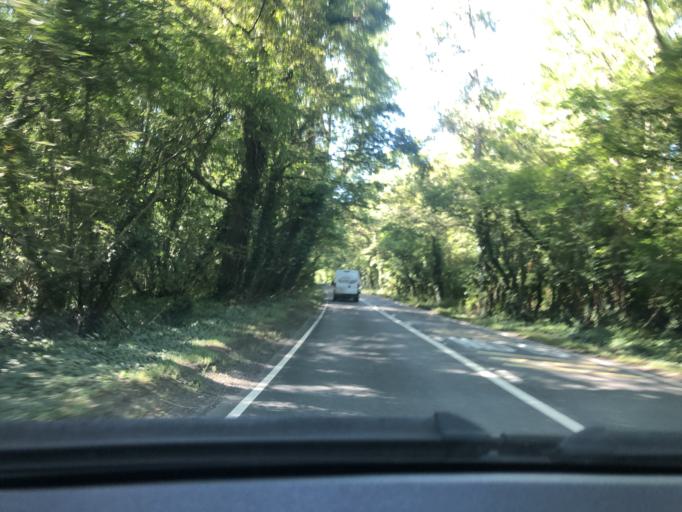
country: GB
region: England
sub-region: Somerset
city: Westonzoyland
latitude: 51.1345
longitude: -2.8540
